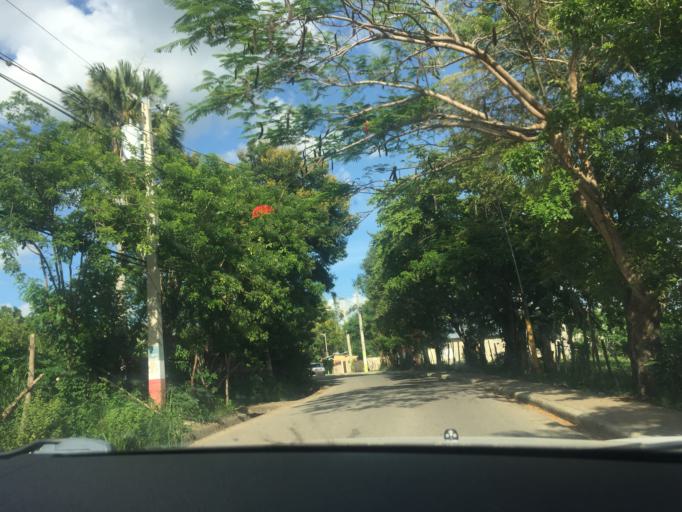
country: DO
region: Santiago
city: Tamboril
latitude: 19.4976
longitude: -70.6364
